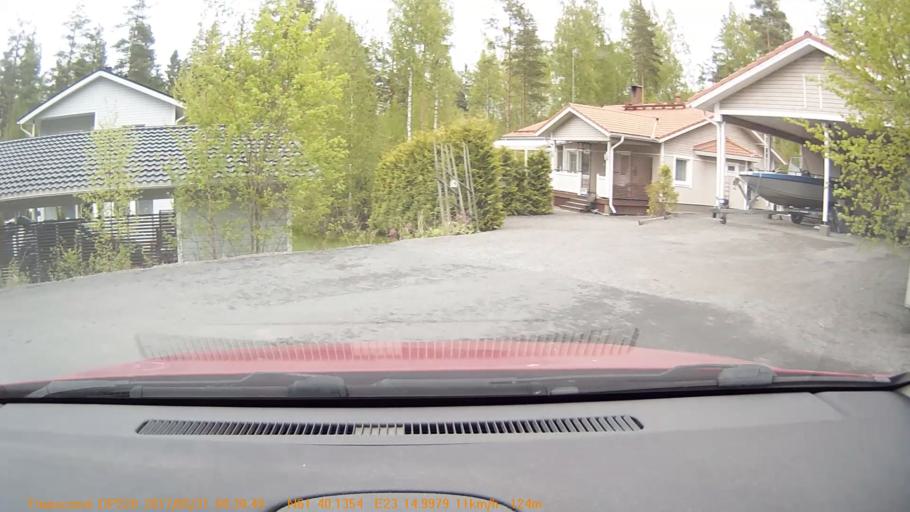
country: FI
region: Pirkanmaa
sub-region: Tampere
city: Viljakkala
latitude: 61.6689
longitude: 23.2500
